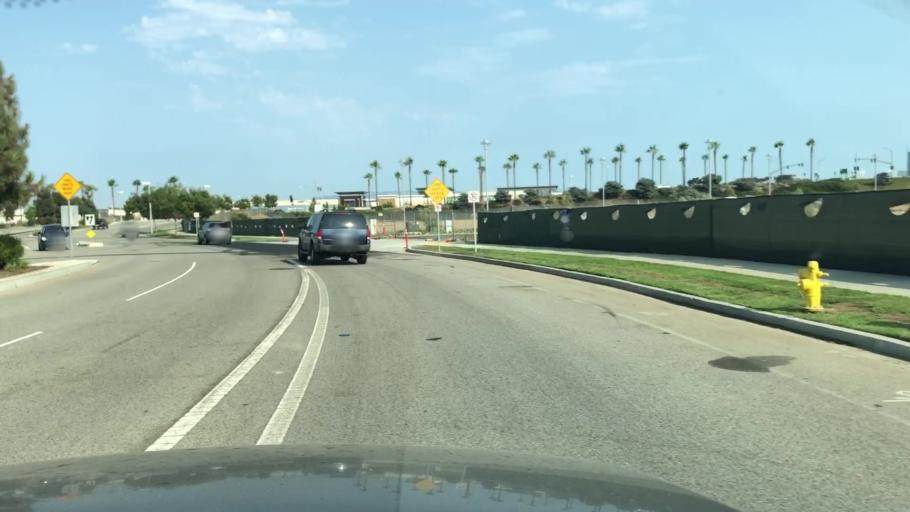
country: US
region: California
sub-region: Ventura County
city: El Rio
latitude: 34.2424
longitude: -119.1827
